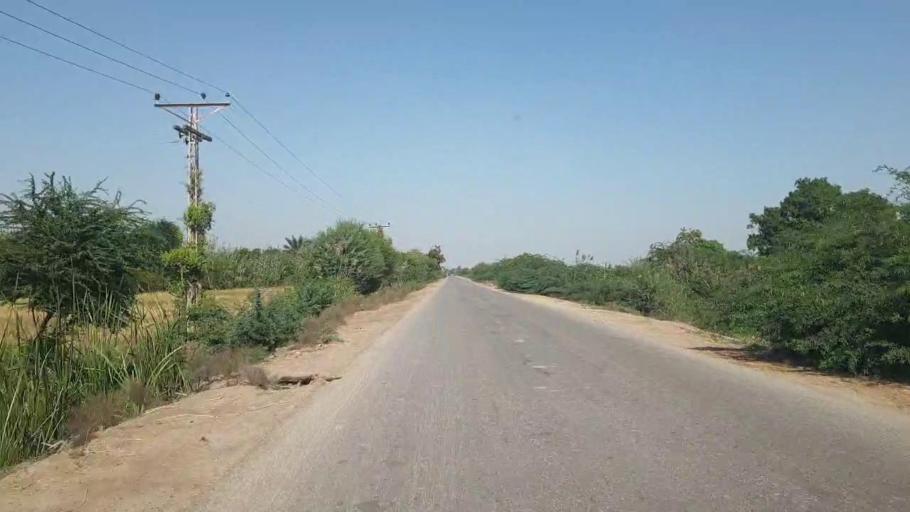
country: PK
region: Sindh
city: Talhar
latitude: 24.9147
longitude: 68.8584
